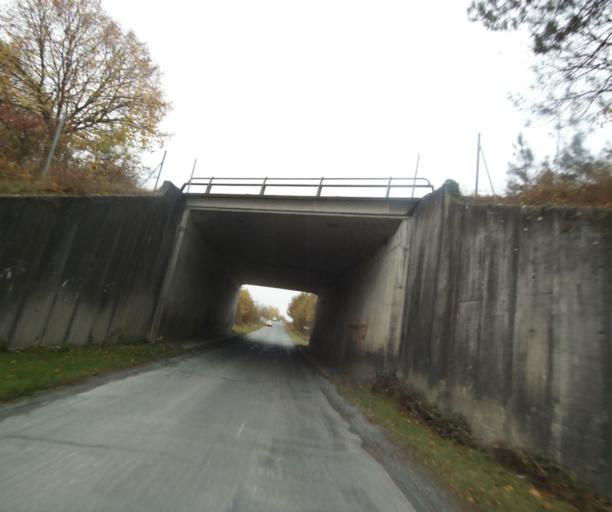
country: FR
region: Poitou-Charentes
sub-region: Departement de la Charente-Maritime
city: Saintes
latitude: 45.7542
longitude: -0.6685
